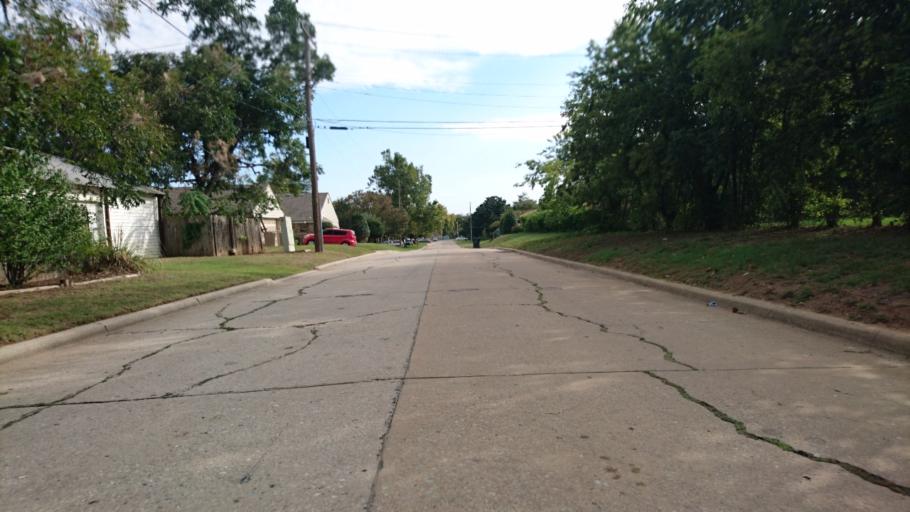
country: US
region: Oklahoma
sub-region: Oklahoma County
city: Nichols Hills
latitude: 35.5098
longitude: -97.5617
